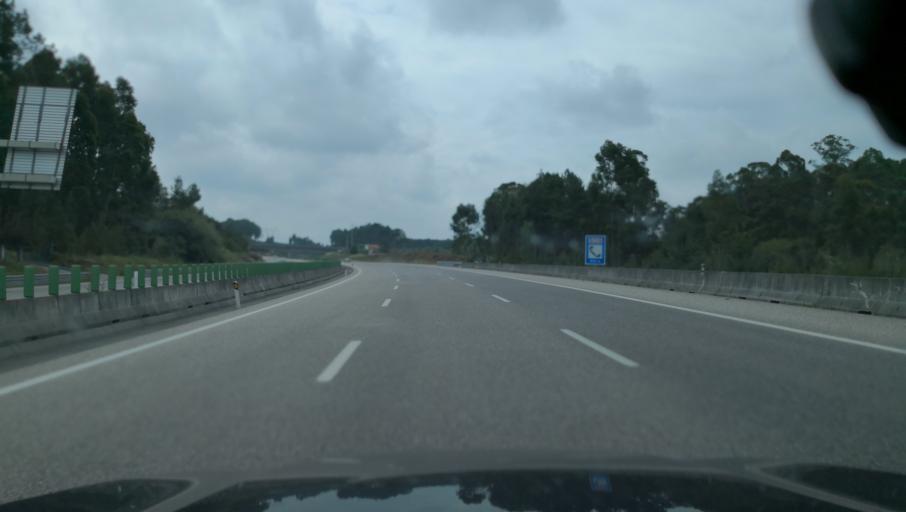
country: PT
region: Leiria
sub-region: Pombal
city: Lourical
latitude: 39.9705
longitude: -8.7817
